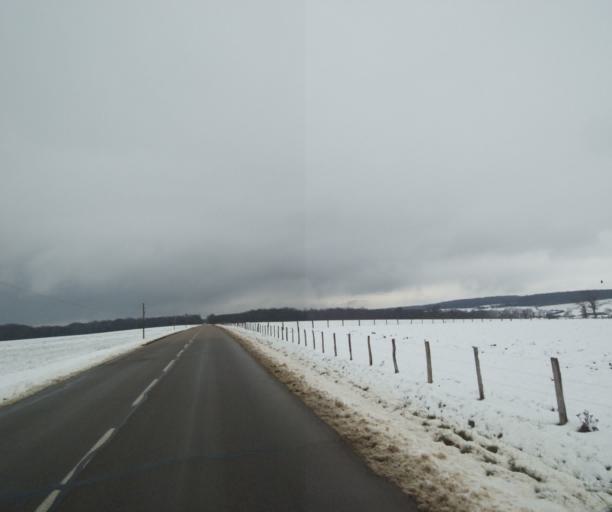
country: FR
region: Champagne-Ardenne
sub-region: Departement de la Haute-Marne
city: Laneuville-a-Remy
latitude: 48.4219
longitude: 4.8400
